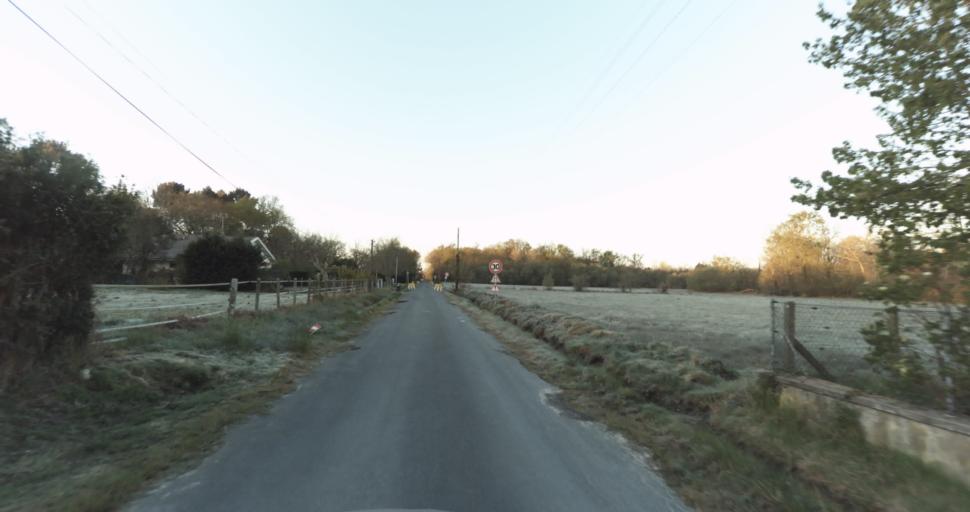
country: FR
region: Aquitaine
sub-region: Departement de la Gironde
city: Martignas-sur-Jalle
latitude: 44.8203
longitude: -0.7433
